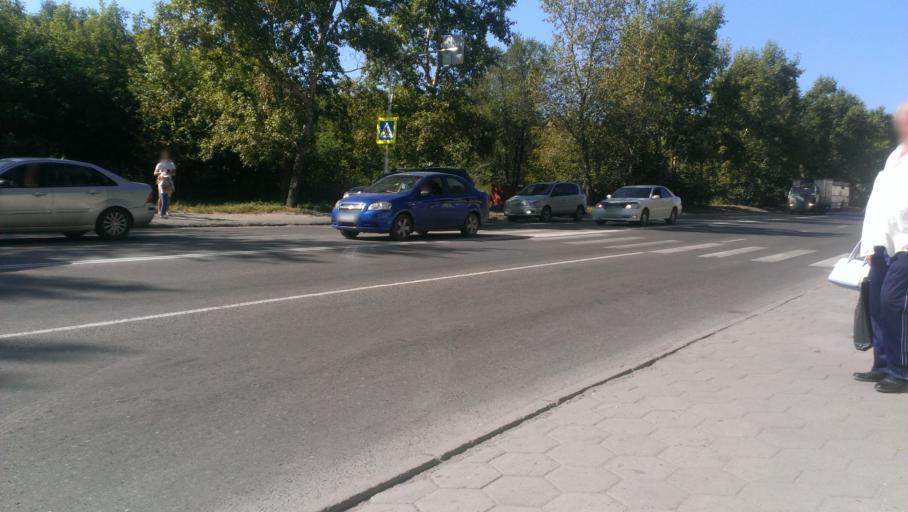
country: RU
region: Altai Krai
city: Novosilikatnyy
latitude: 53.3691
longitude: 83.6620
